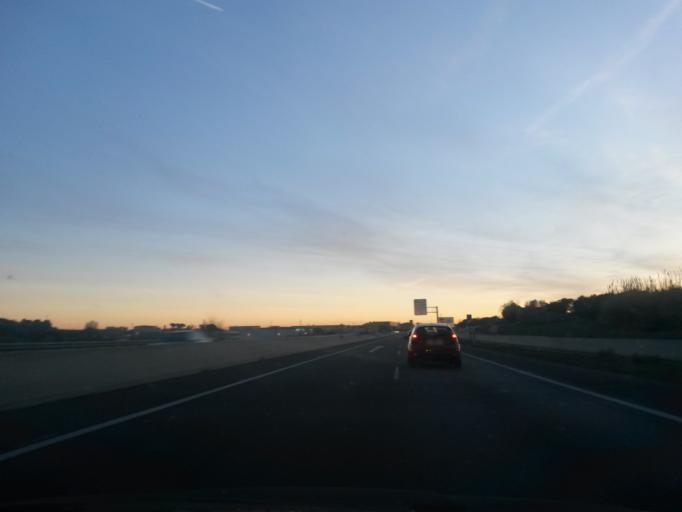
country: ES
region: Catalonia
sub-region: Provincia de Girona
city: Riudellots de la Selva
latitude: 41.9102
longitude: 2.7900
